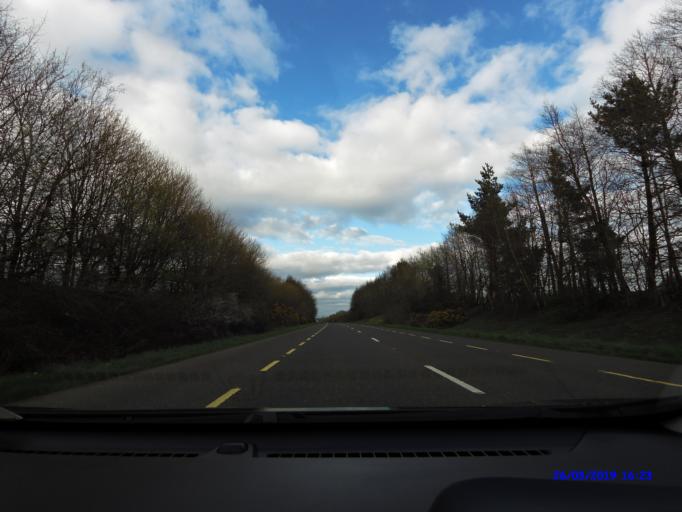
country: IE
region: Connaught
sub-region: Maigh Eo
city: Swinford
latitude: 53.9325
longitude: -8.9462
